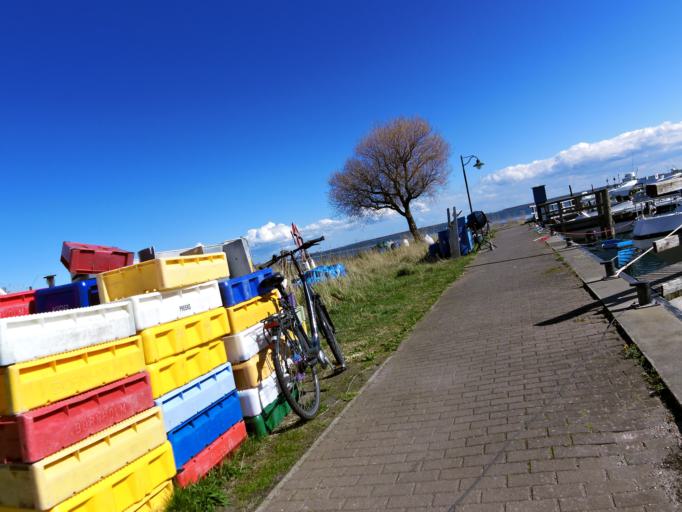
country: DE
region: Mecklenburg-Vorpommern
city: Hiddensee
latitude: 54.5247
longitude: 13.0933
